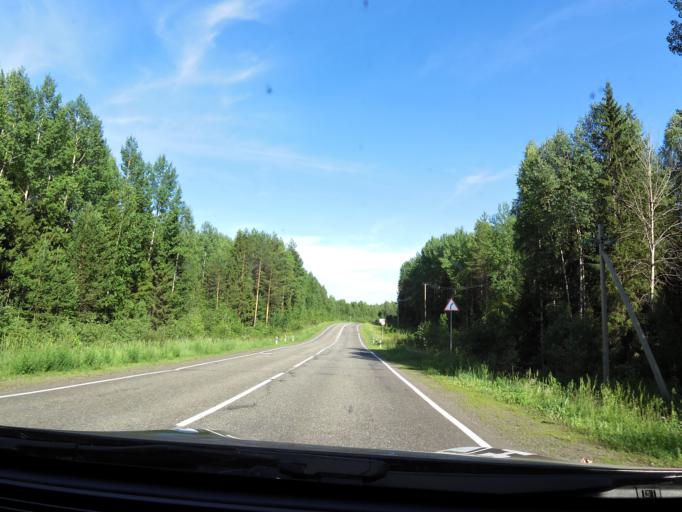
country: RU
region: Kirov
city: Dubrovka
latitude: 58.9134
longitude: 51.1639
